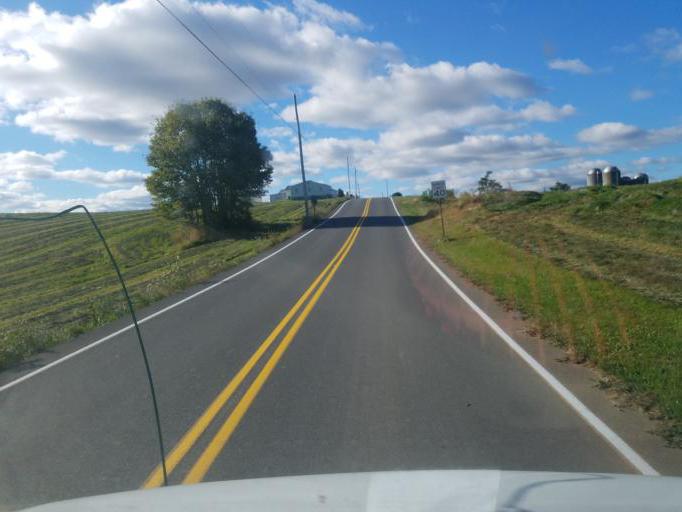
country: US
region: Pennsylvania
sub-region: Franklin County
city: Guilford Siding
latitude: 39.8239
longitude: -77.6391
